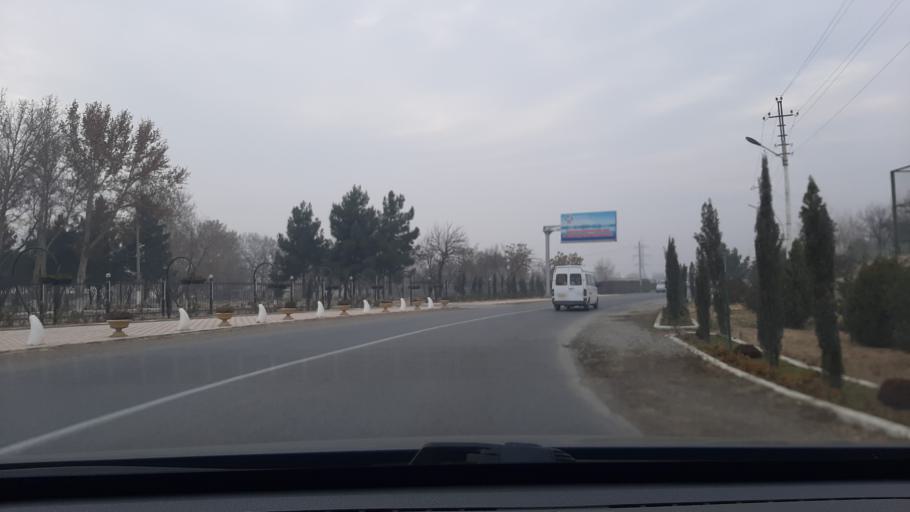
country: TJ
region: Viloyati Sughd
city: Palos
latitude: 40.2712
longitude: 69.8126
